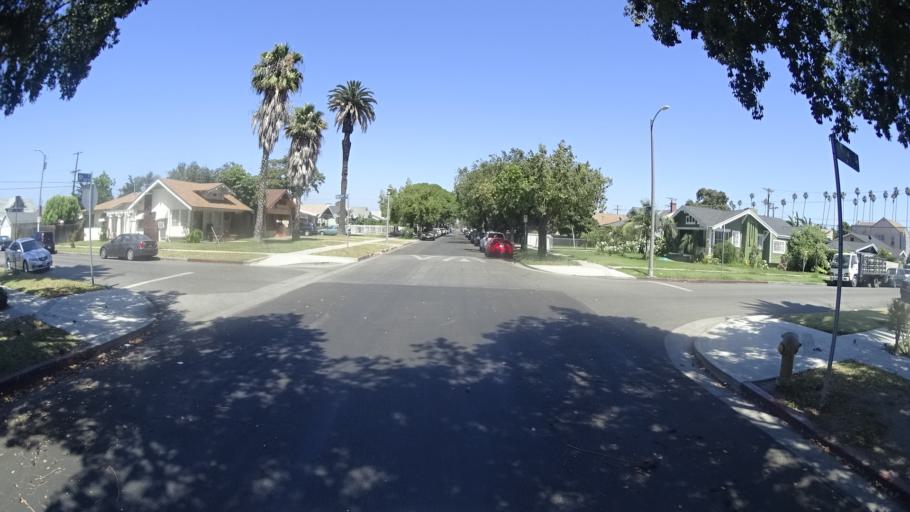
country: US
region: California
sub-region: Los Angeles County
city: View Park-Windsor Hills
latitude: 33.9982
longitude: -118.3070
